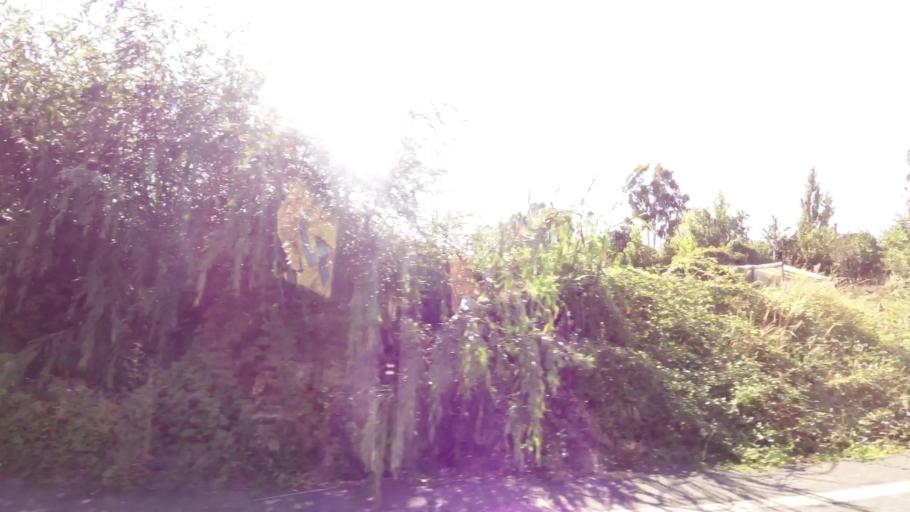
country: CL
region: Maule
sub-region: Provincia de Talca
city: Talca
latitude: -35.4068
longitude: -71.5937
